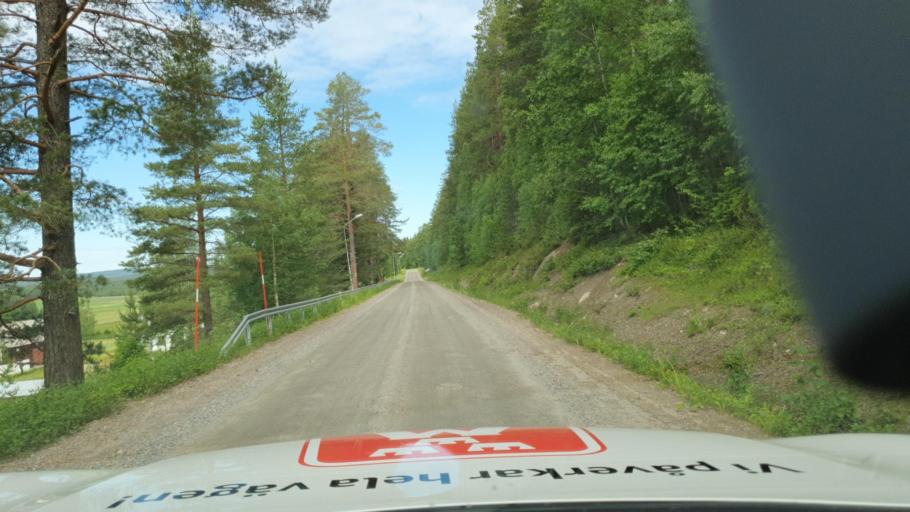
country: SE
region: Vaesterbotten
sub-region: Skelleftea Kommun
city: Forsbacka
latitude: 64.6550
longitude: 20.5378
